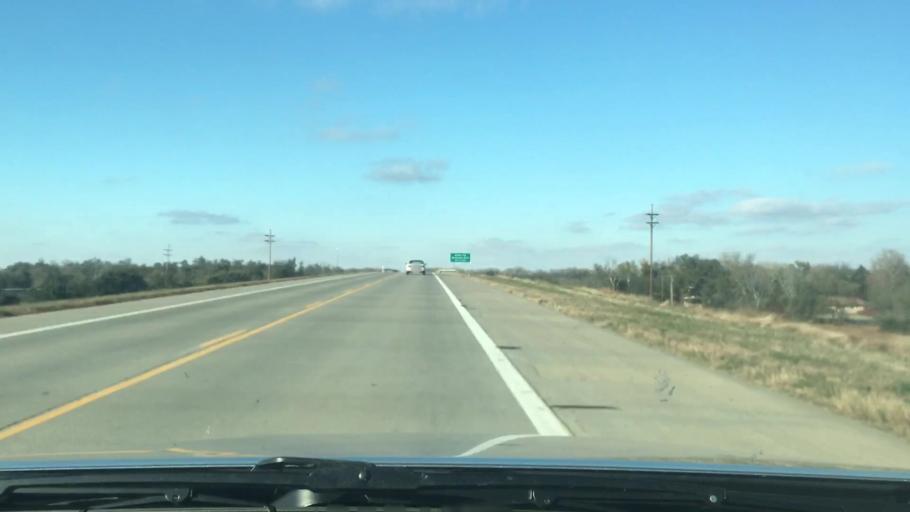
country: US
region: Kansas
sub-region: Reno County
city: Hutchinson
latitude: 38.0802
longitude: -97.9890
